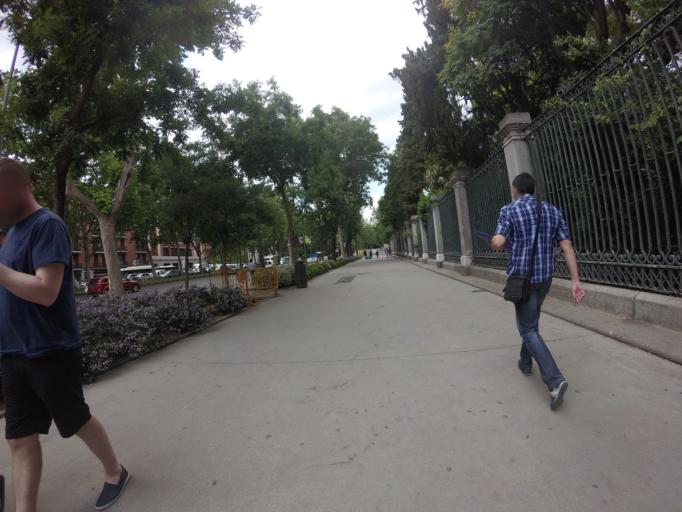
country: ES
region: Madrid
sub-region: Provincia de Madrid
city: Retiro
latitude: 40.4101
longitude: -3.6921
